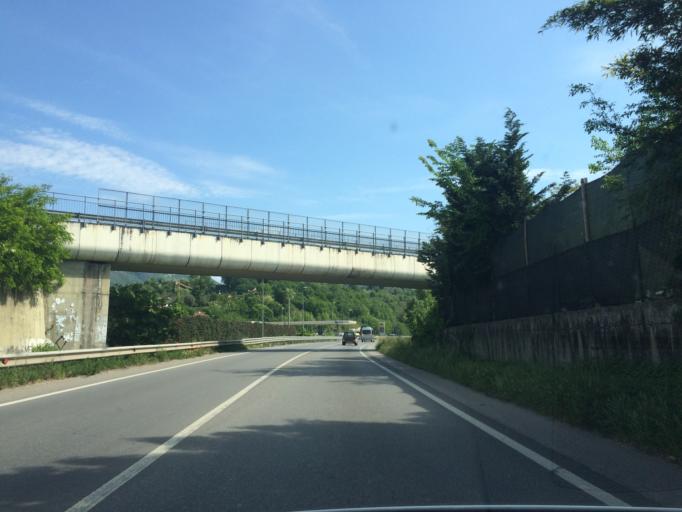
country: IT
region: Lombardy
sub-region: Provincia di Brescia
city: Gavardo-Sopraponte
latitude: 45.5814
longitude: 10.4488
